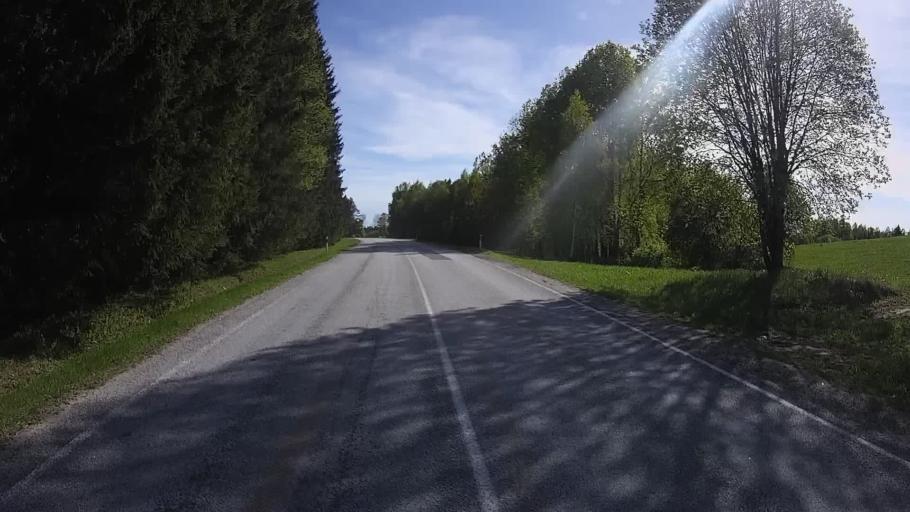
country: EE
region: Vorumaa
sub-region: Antsla vald
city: Vana-Antsla
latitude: 58.0159
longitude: 26.4990
